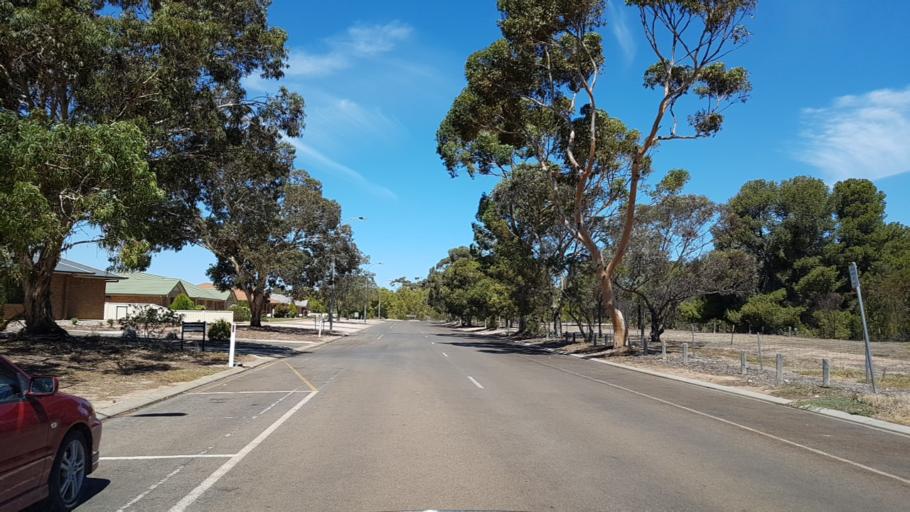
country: AU
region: South Australia
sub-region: Copper Coast
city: Wallaroo
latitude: -34.0620
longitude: 137.5898
